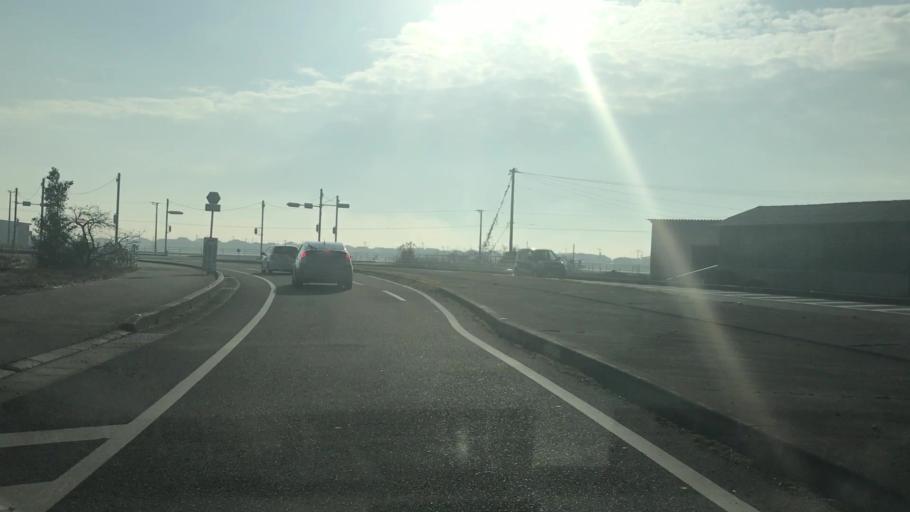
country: JP
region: Saga Prefecture
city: Saga-shi
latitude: 33.2179
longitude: 130.1705
